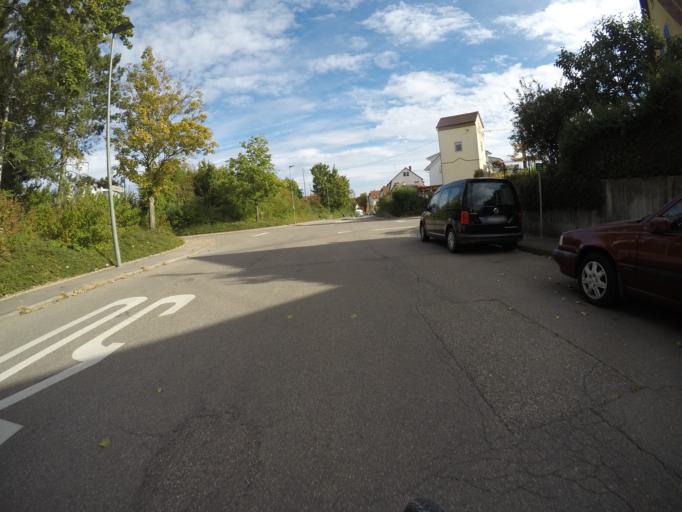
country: DE
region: Baden-Wuerttemberg
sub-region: Regierungsbezirk Stuttgart
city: Leonberg
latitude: 48.8190
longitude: 9.0118
